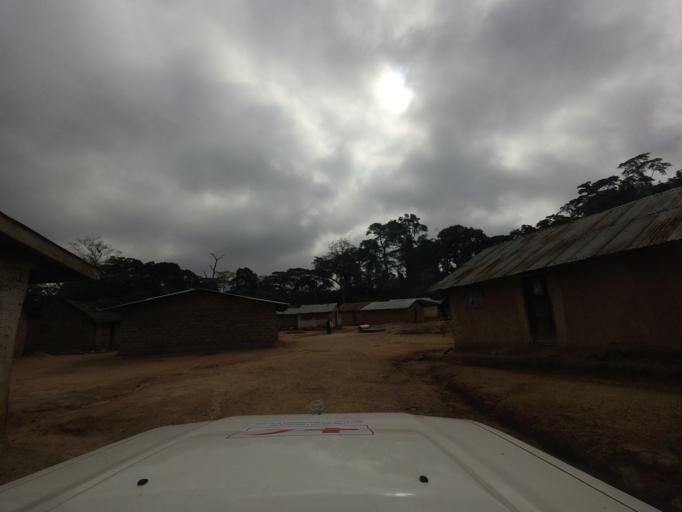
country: LR
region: Lofa
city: Voinjama
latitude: 8.4625
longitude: -9.7891
